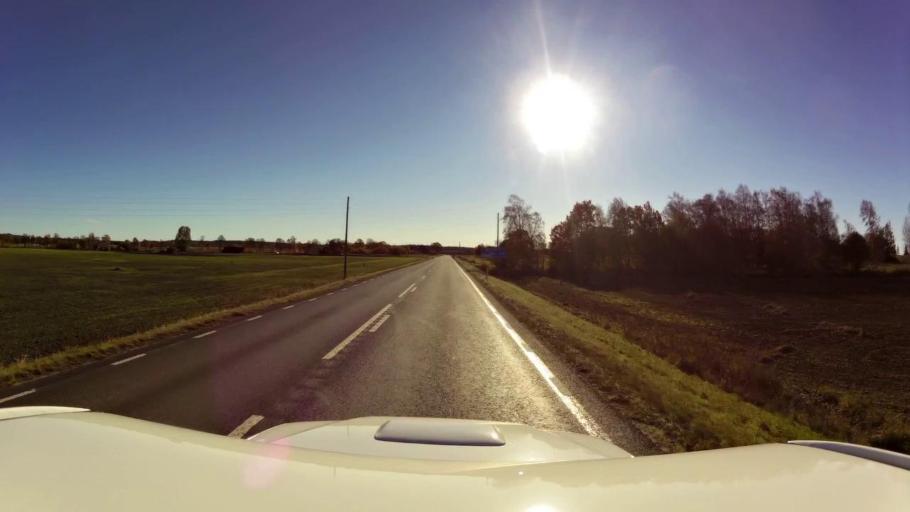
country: SE
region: OEstergoetland
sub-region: Linkopings Kommun
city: Ljungsbro
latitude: 58.5225
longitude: 15.4204
